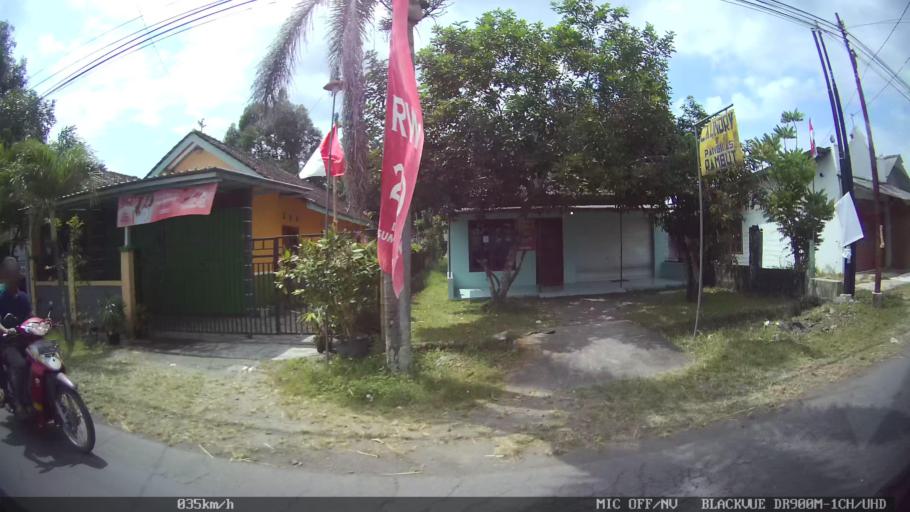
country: ID
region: Daerah Istimewa Yogyakarta
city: Depok
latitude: -7.7984
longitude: 110.4559
